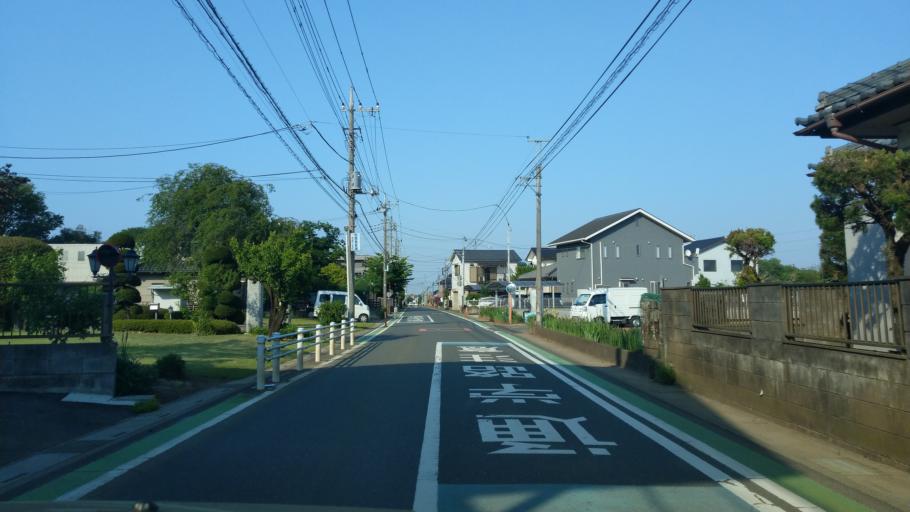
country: JP
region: Saitama
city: Tokorozawa
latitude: 35.8332
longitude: 139.4829
